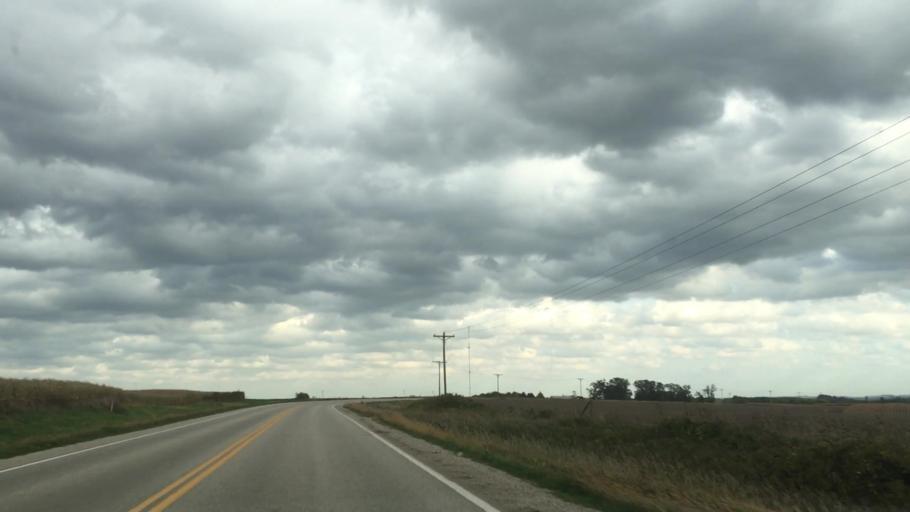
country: US
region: Minnesota
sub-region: Fillmore County
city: Preston
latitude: 43.7353
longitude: -92.1023
